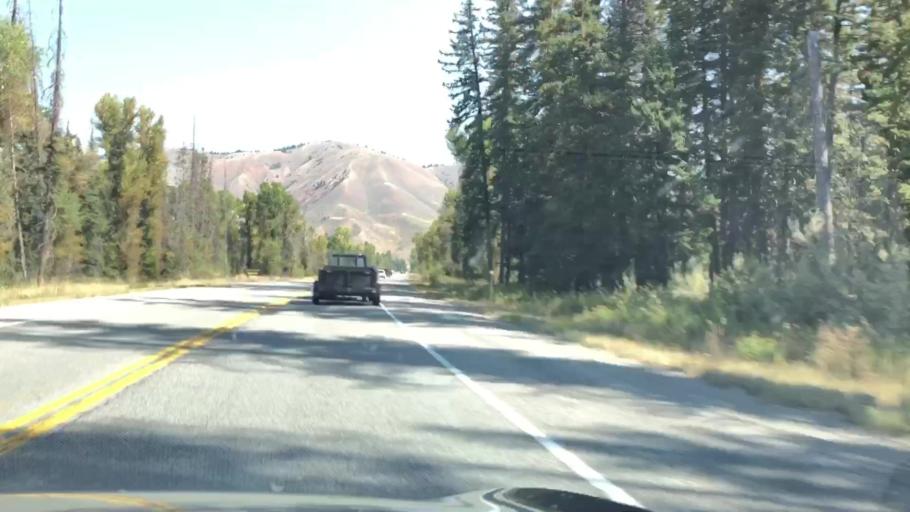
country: US
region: Wyoming
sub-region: Teton County
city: Hoback
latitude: 43.2864
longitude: -110.7964
